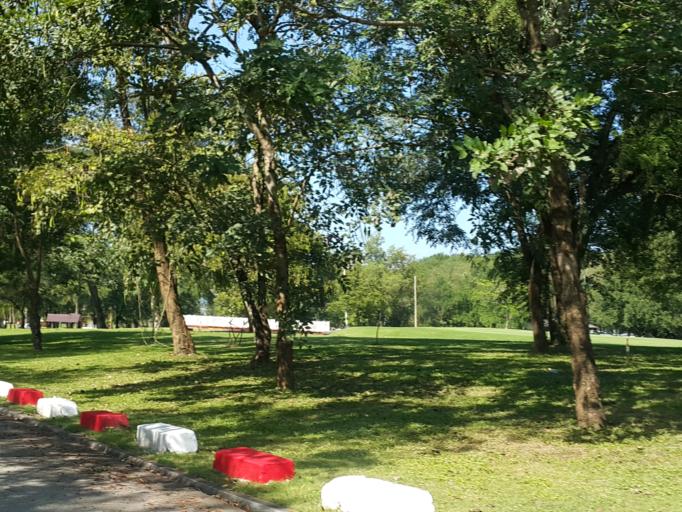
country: TH
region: Lampang
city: Mae Mo
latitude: 18.3206
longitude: 99.7448
